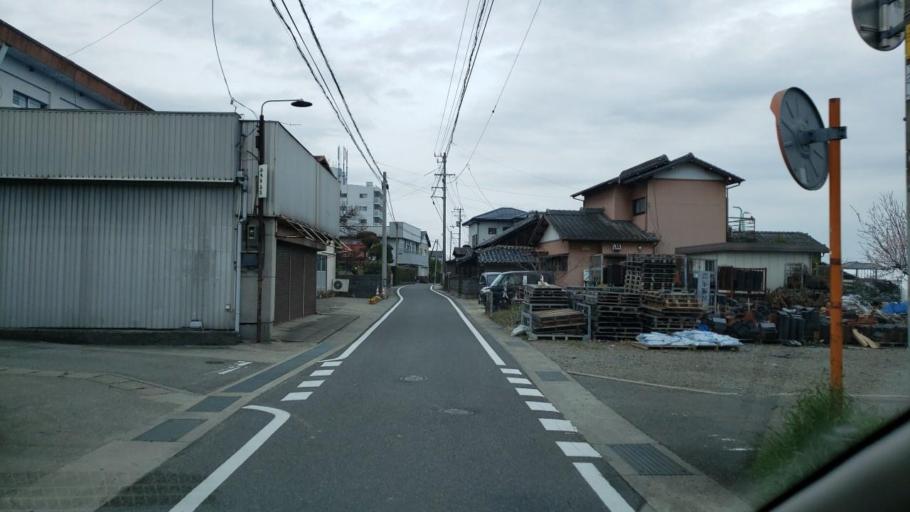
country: JP
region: Tokushima
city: Kamojimacho-jogejima
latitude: 34.0890
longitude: 134.2935
